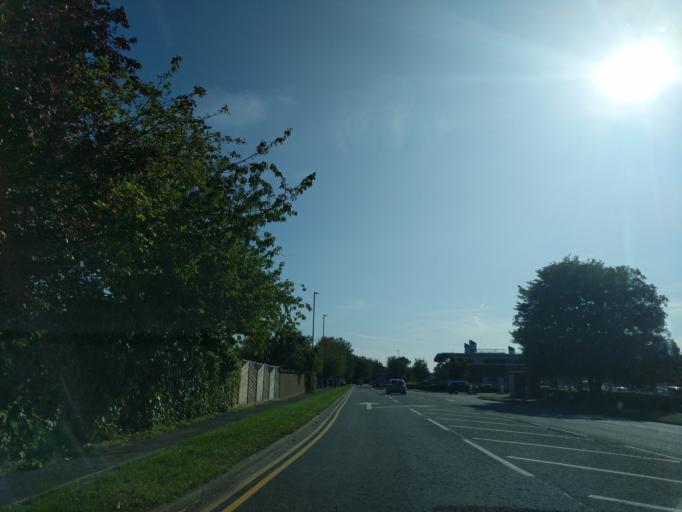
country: GB
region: England
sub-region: Lincolnshire
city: Bourne
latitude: 52.7603
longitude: -0.3689
